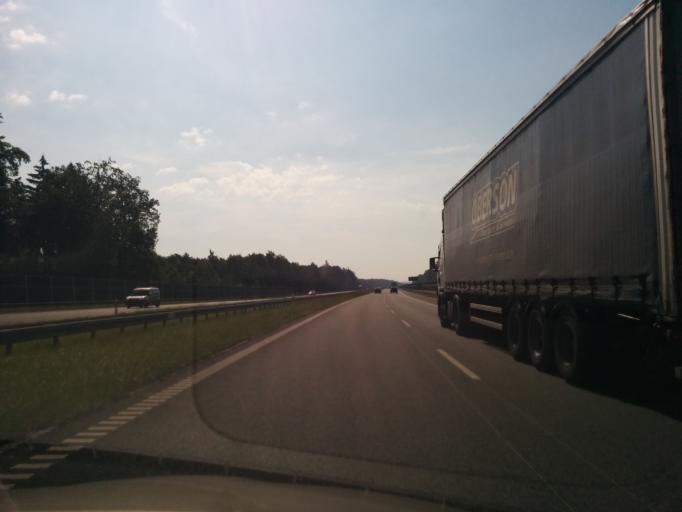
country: PL
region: Silesian Voivodeship
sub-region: Powiat tarnogorski
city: Radzionkow
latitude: 50.3864
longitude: 18.8502
